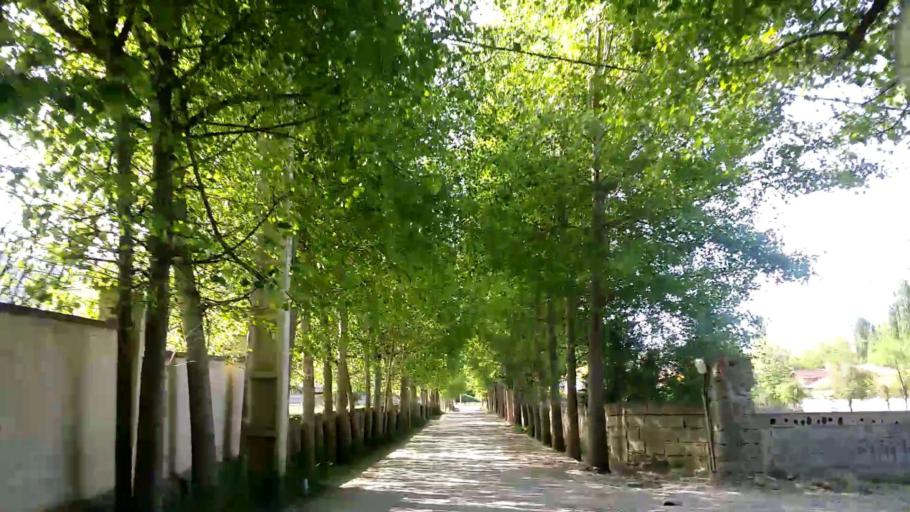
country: IR
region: Mazandaran
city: `Abbasabad
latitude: 36.5196
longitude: 51.1740
